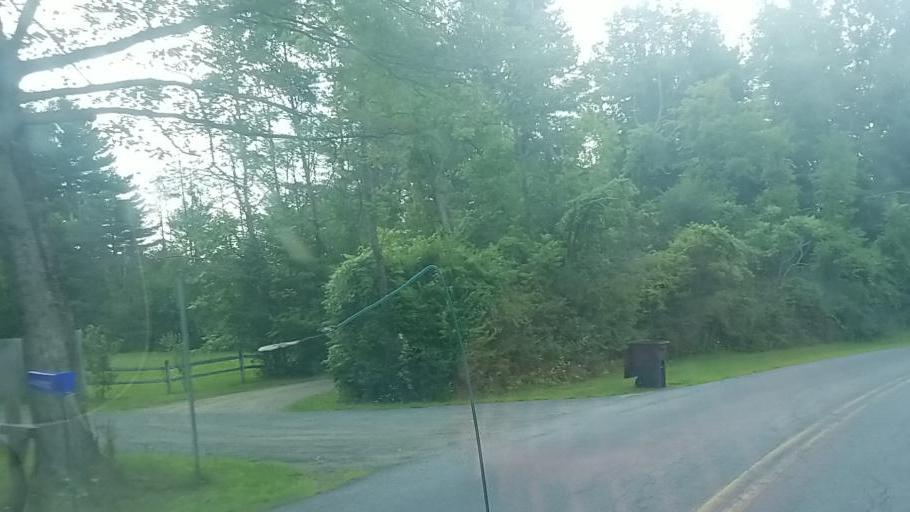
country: US
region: New York
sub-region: Fulton County
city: Broadalbin
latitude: 43.0781
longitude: -74.2232
